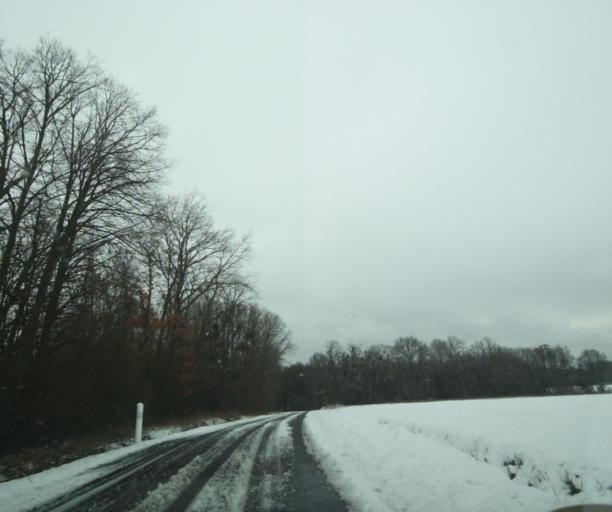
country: FR
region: Champagne-Ardenne
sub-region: Departement de la Haute-Marne
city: Montier-en-Der
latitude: 48.4273
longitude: 4.7284
